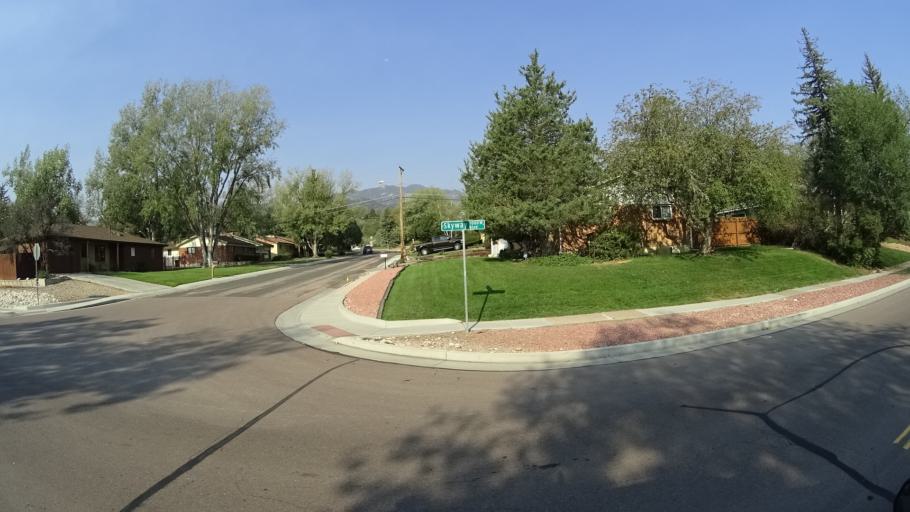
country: US
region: Colorado
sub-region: El Paso County
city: Colorado Springs
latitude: 38.8113
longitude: -104.8460
